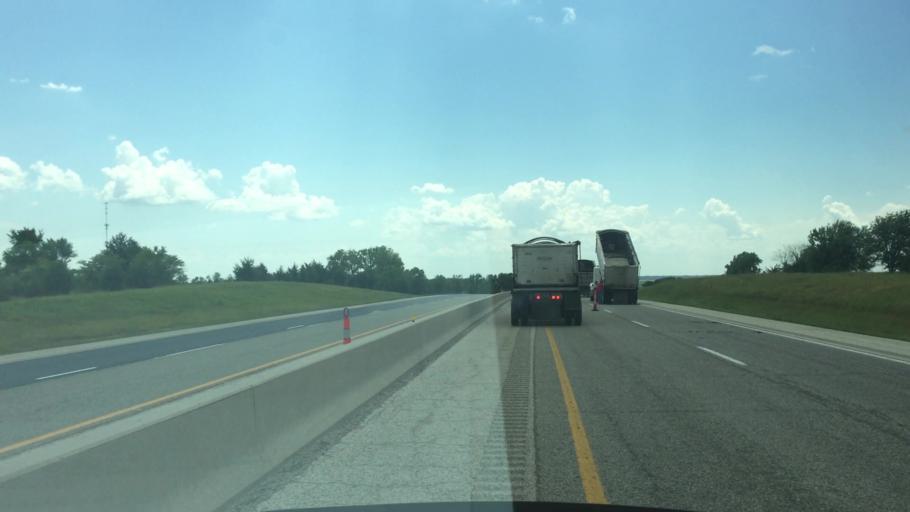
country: US
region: Kansas
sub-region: Shawnee County
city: Auburn
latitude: 38.8060
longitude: -95.9009
